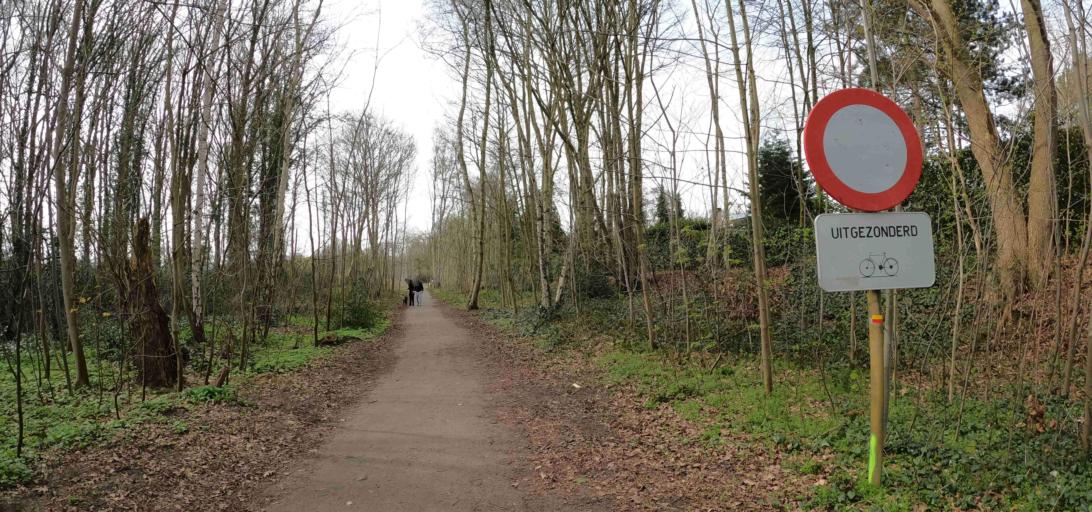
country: BE
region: Flanders
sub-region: Provincie Oost-Vlaanderen
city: Waasmunster
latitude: 51.1160
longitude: 4.0969
